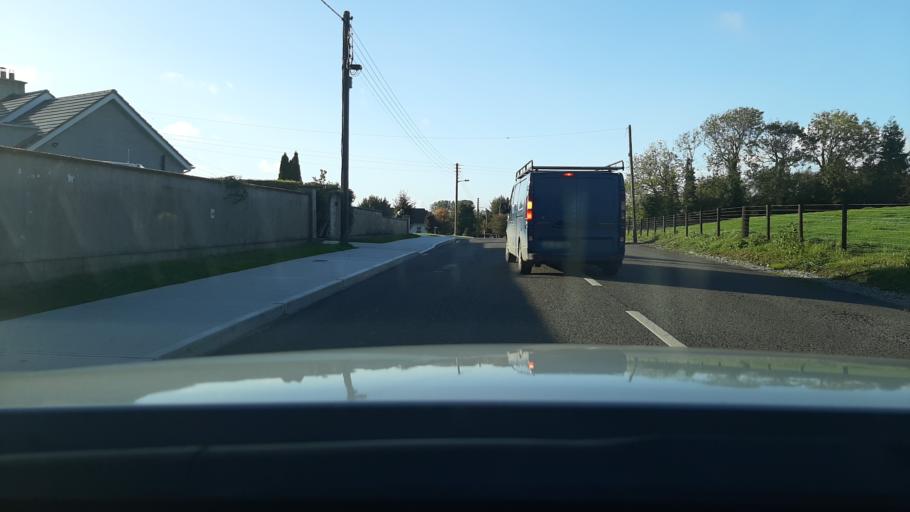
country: IE
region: Leinster
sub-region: Kildare
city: Rathangan
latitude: 53.2224
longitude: -6.9985
